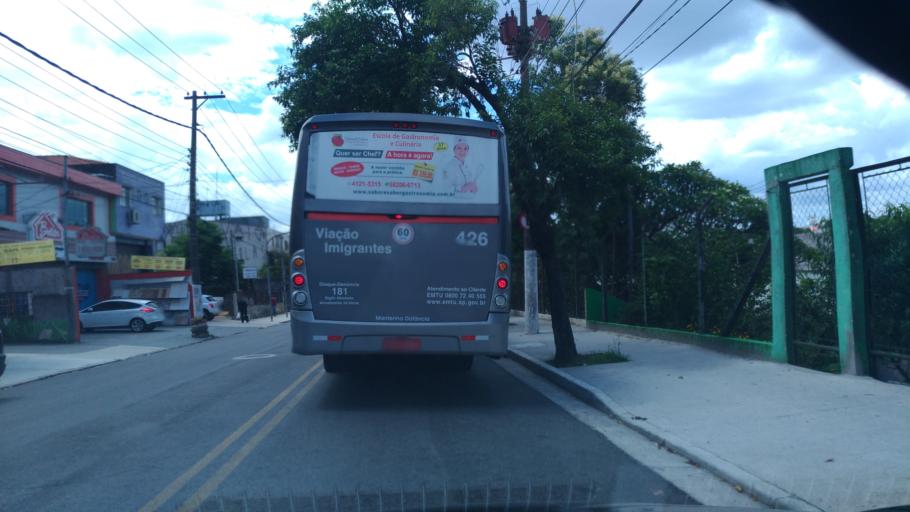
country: BR
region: Sao Paulo
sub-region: Sao Bernardo Do Campo
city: Sao Bernardo do Campo
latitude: -23.7111
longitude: -46.5877
